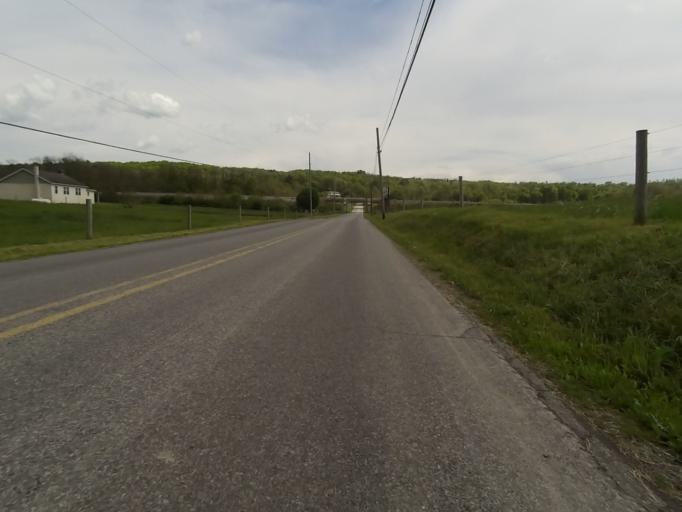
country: US
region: Pennsylvania
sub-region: Centre County
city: Zion
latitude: 40.9810
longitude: -77.6291
